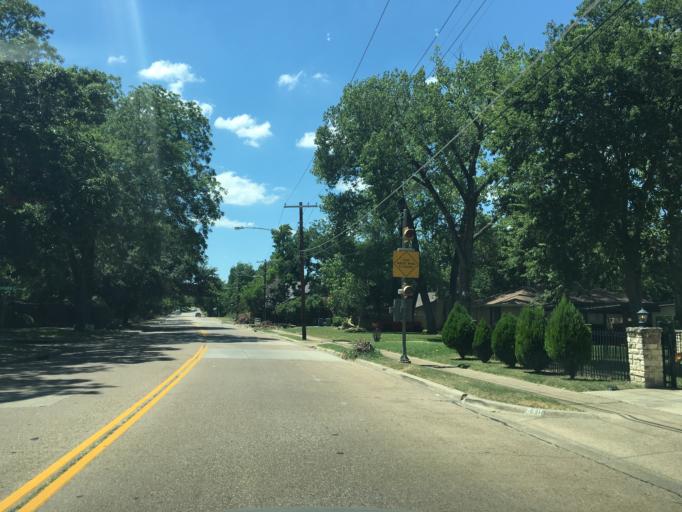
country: US
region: Texas
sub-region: Dallas County
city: Highland Park
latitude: 32.8438
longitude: -96.7026
